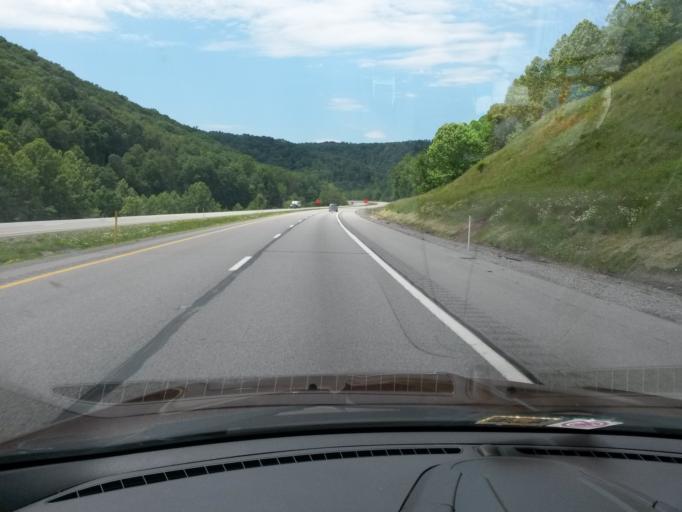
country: US
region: West Virginia
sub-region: Braxton County
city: Sutton
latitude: 38.7718
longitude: -80.6758
